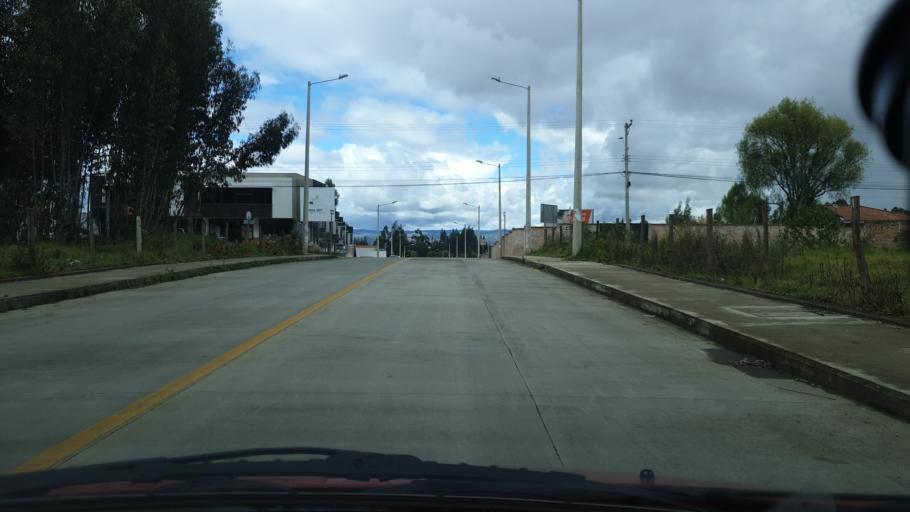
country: EC
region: Azuay
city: Cuenca
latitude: -2.8820
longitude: -79.0517
